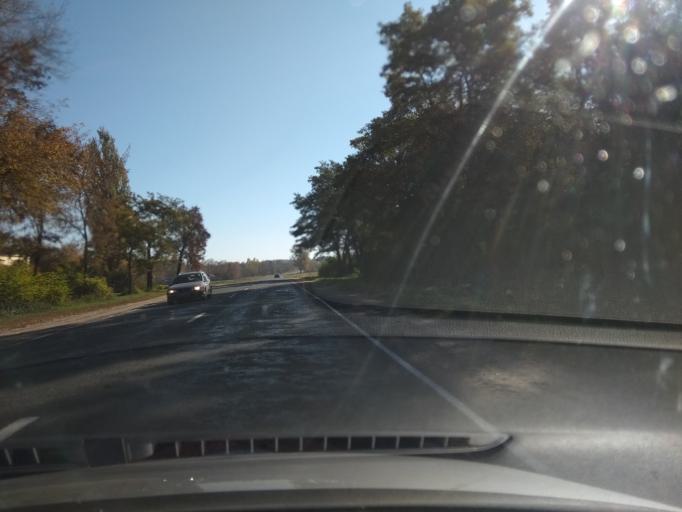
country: BY
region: Brest
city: Malaryta
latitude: 51.9292
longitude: 24.0641
